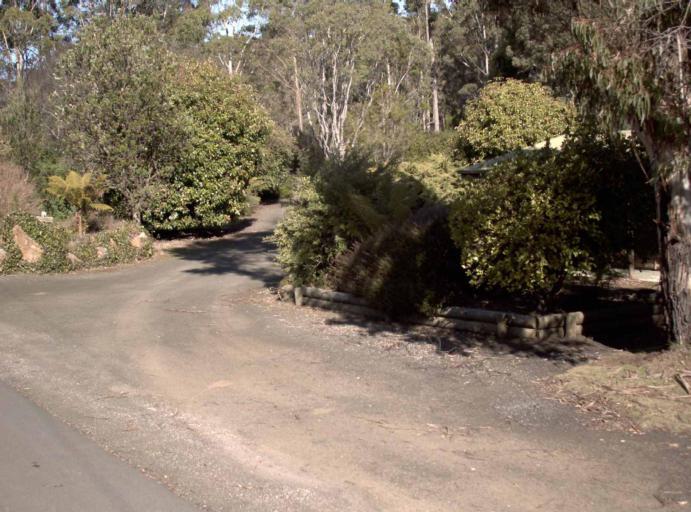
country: AU
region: Tasmania
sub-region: Launceston
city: Mayfield
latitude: -41.3128
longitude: 147.2000
